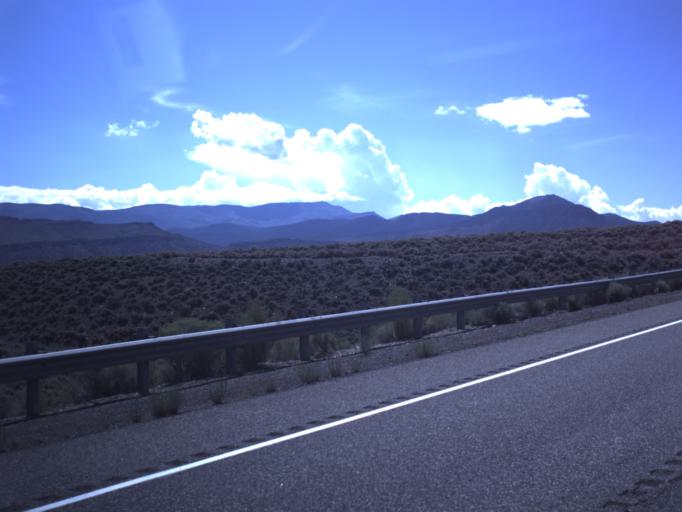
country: US
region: Utah
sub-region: Piute County
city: Junction
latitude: 38.3447
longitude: -112.2186
